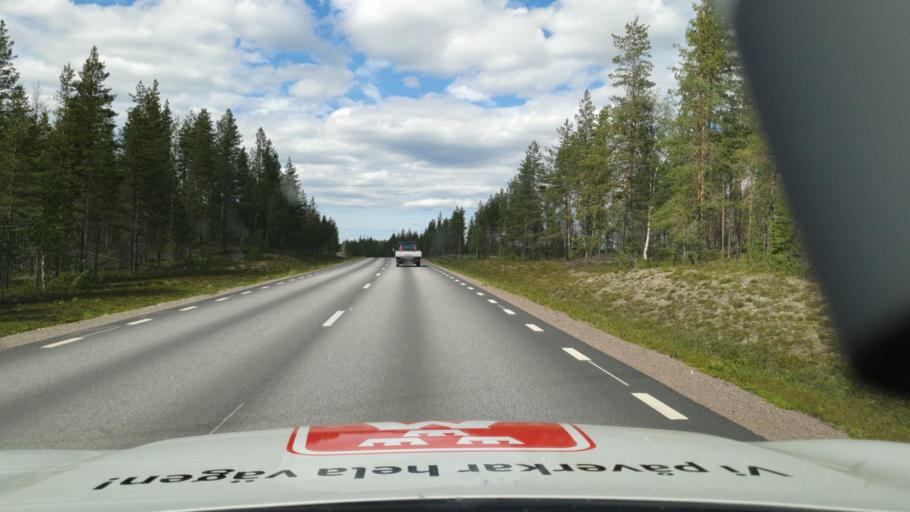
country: SE
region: Vaesterbotten
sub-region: Skelleftea Kommun
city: Langsele
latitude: 65.0862
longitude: 20.0019
